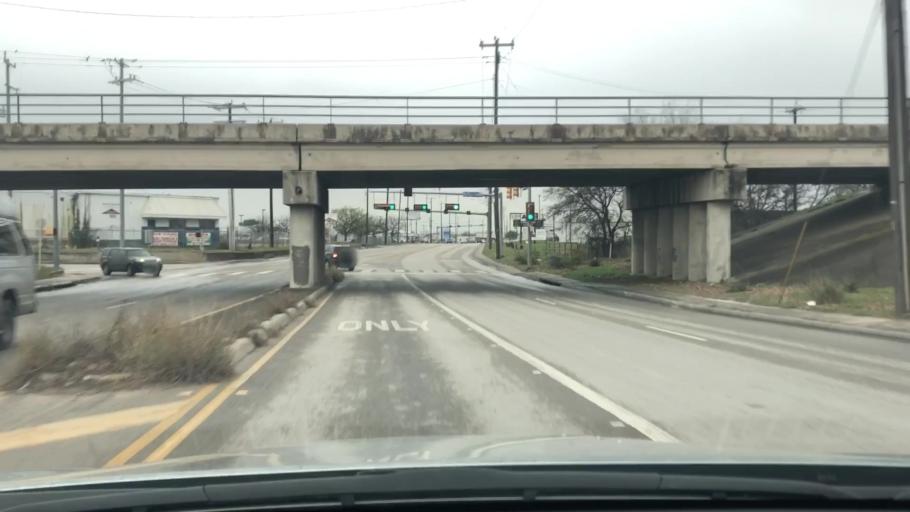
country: US
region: Texas
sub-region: Bexar County
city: Terrell Hills
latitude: 29.4390
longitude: -98.4358
